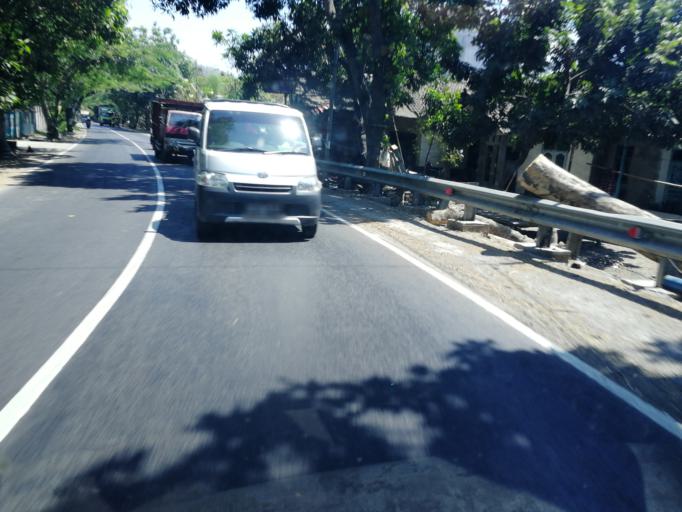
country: ID
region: West Nusa Tenggara
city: Jelateng Timur
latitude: -8.6987
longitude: 116.1058
